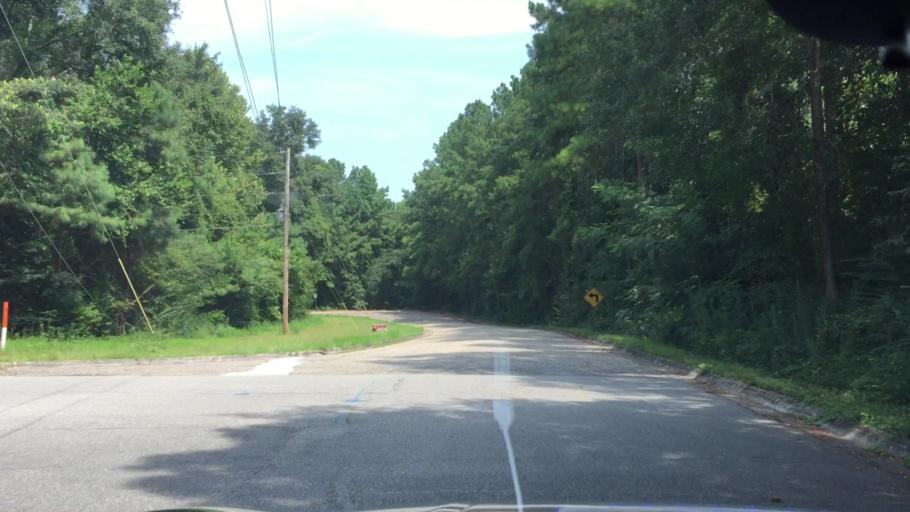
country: US
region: Alabama
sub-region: Coffee County
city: Enterprise
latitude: 31.3345
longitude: -85.8122
